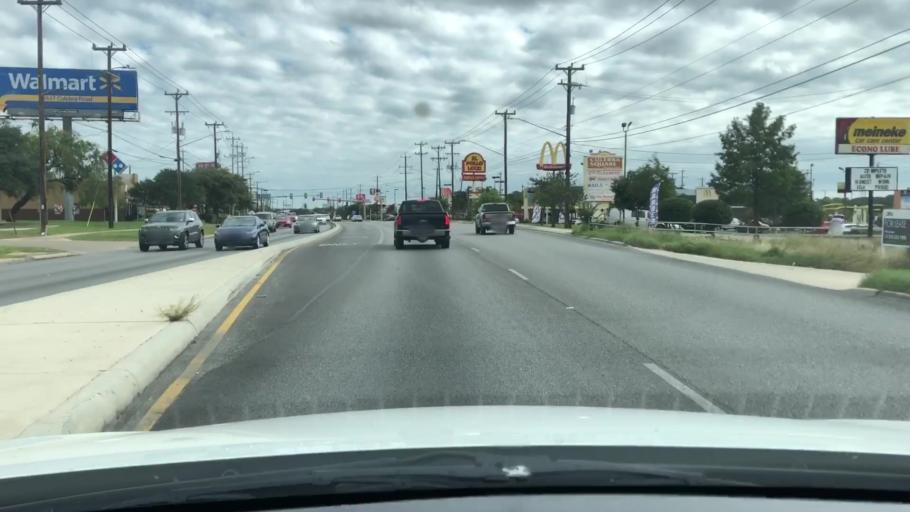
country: US
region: Texas
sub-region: Bexar County
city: Leon Valley
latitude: 29.4855
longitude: -98.6685
